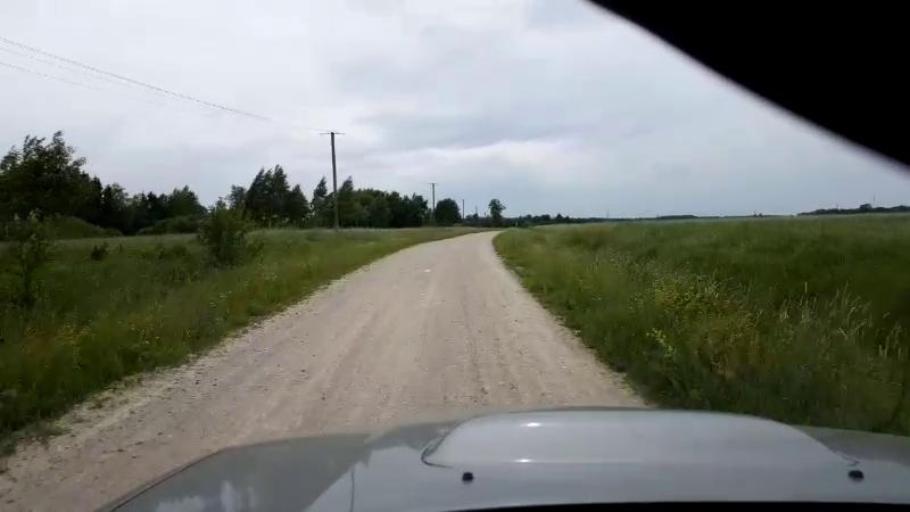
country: EE
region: Paernumaa
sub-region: Sindi linn
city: Sindi
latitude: 58.5276
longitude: 24.6172
